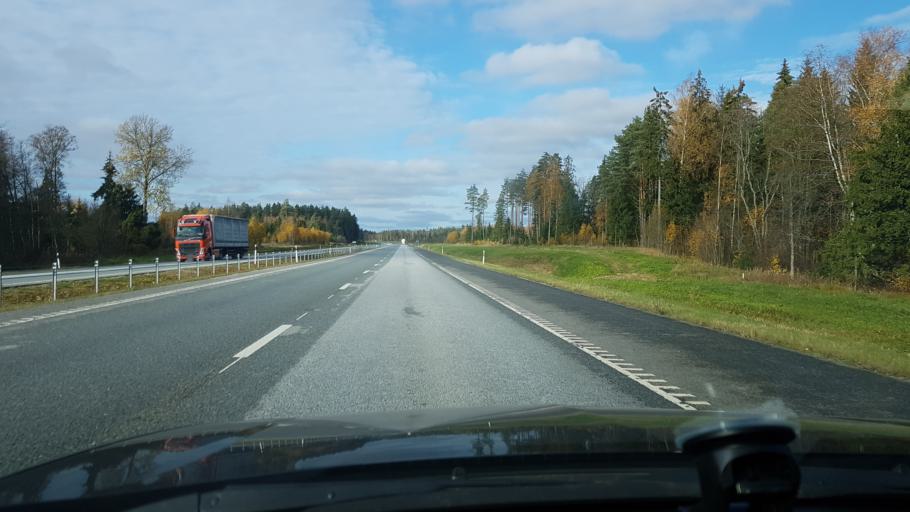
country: EE
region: Laeaene-Virumaa
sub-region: Kadrina vald
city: Kadrina
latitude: 59.4567
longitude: 26.0450
